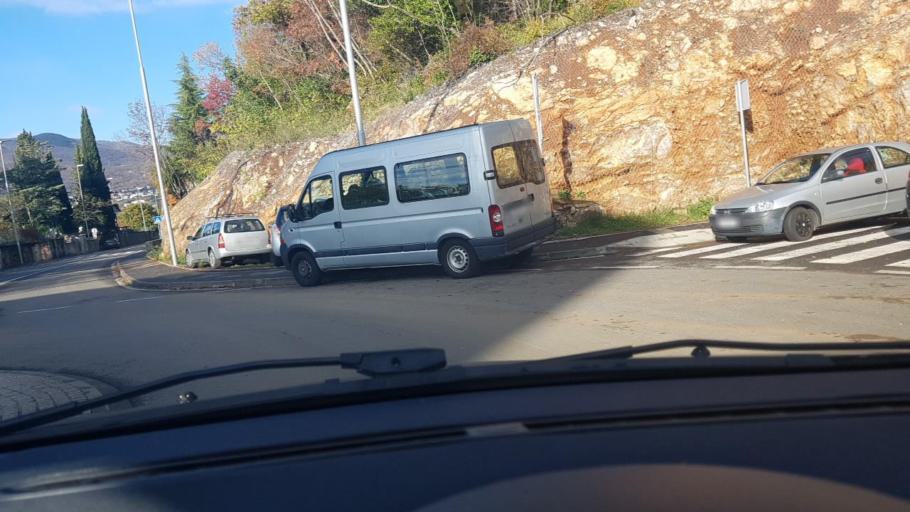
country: HR
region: Primorsko-Goranska
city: Rubesi
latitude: 45.3477
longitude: 14.3496
